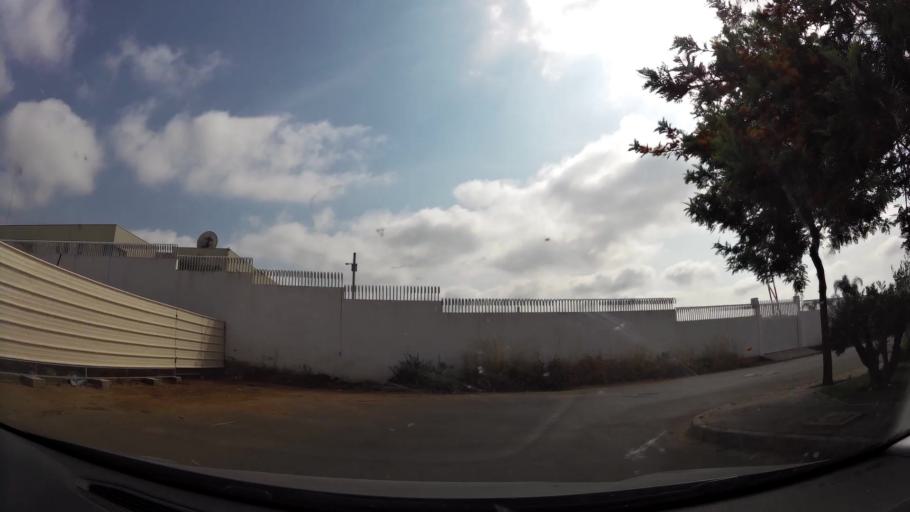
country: MA
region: Rabat-Sale-Zemmour-Zaer
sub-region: Rabat
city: Rabat
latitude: 33.9706
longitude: -6.8469
